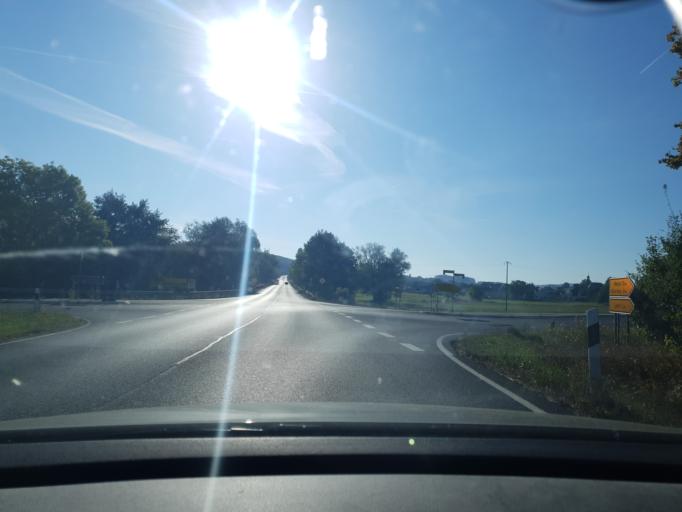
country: DE
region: Hesse
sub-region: Regierungsbezirk Giessen
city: Hoernsheim
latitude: 50.4816
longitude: 8.6089
